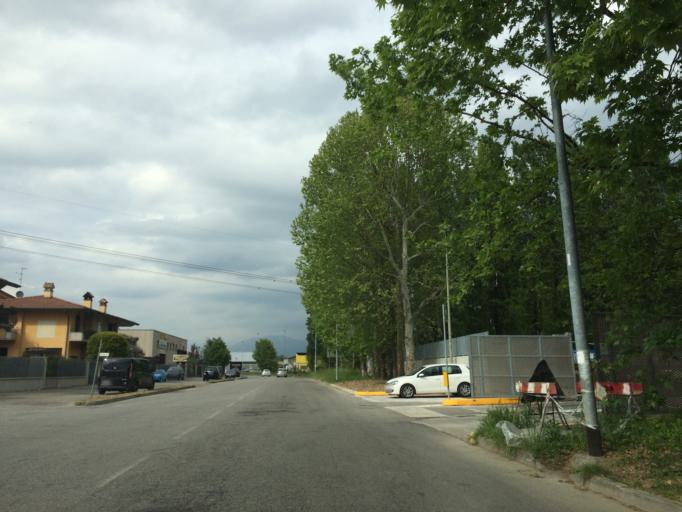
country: IT
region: Lombardy
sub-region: Provincia di Brescia
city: Flero
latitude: 45.4895
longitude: 10.1657
